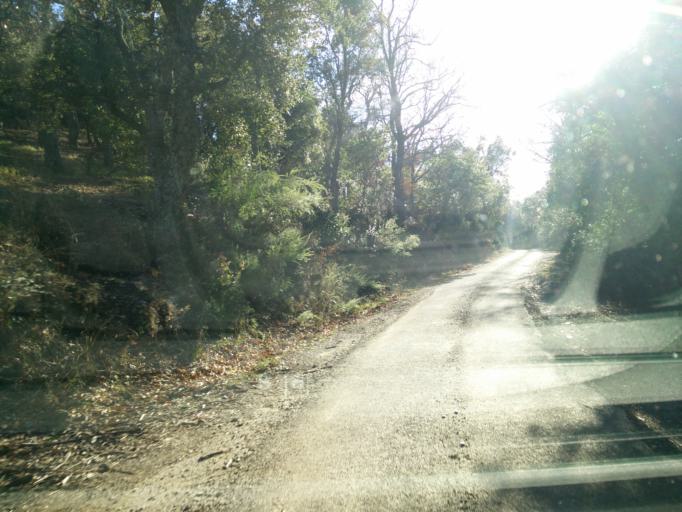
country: FR
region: Provence-Alpes-Cote d'Azur
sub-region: Departement du Var
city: Collobrieres
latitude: 43.2730
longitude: 6.3013
